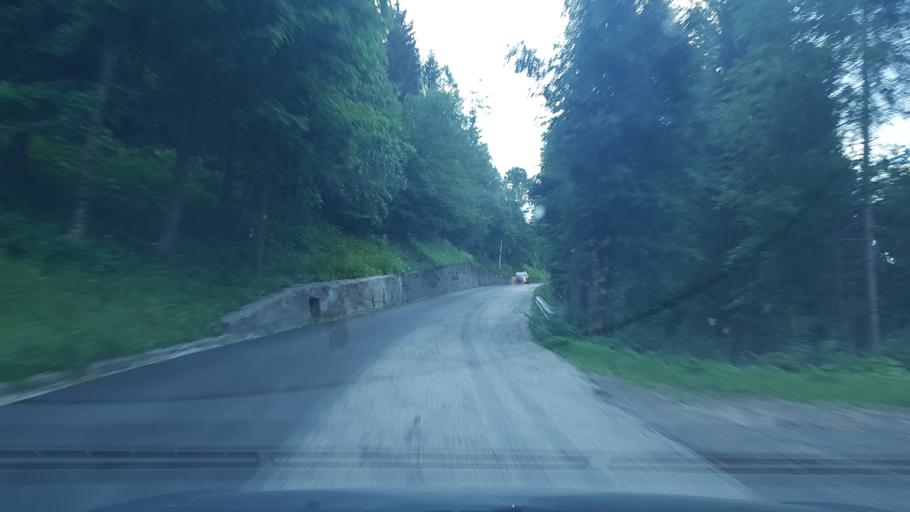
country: IT
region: Friuli Venezia Giulia
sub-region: Provincia di Udine
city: Forni Avoltri
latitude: 46.5832
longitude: 12.7899
